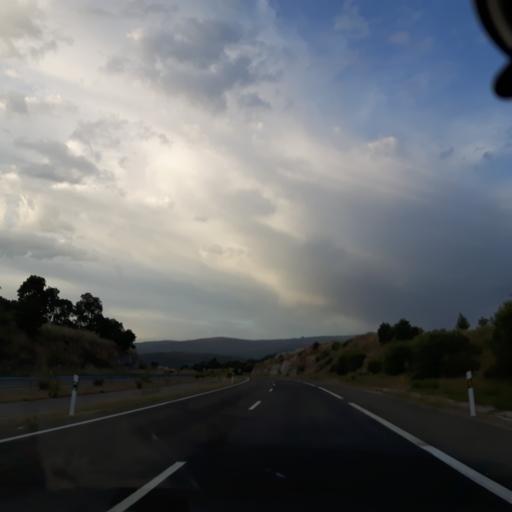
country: ES
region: Castille and Leon
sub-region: Provincia de Salamanca
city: Nava de Bejar
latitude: 40.4731
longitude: -5.6822
